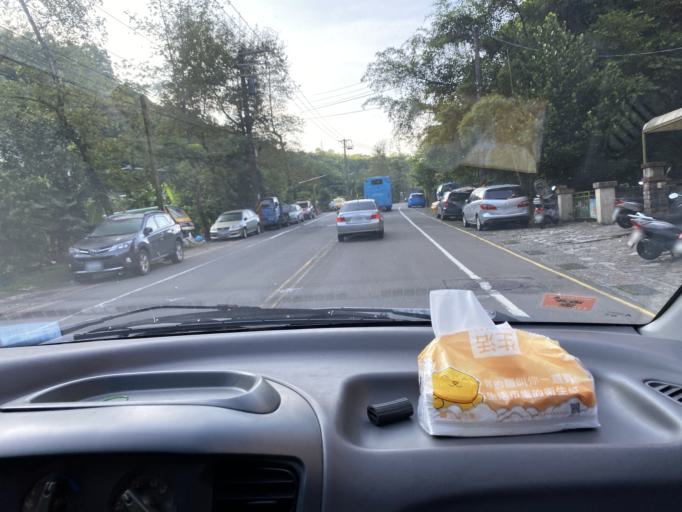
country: TW
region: Taiwan
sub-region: Keelung
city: Keelung
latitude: 25.0982
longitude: 121.7384
